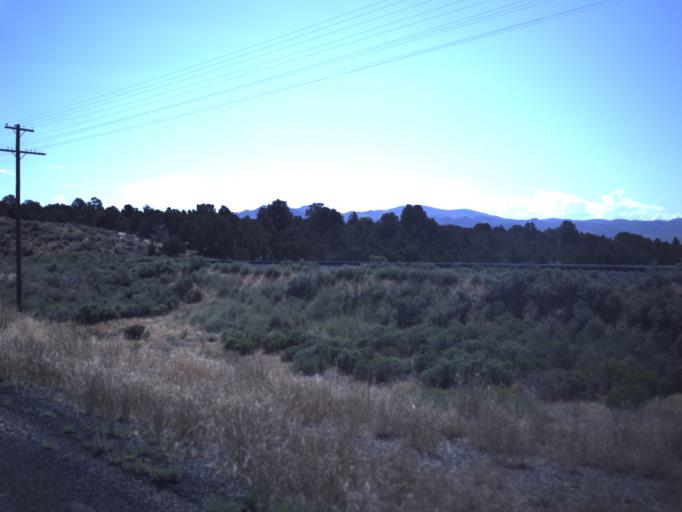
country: US
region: Utah
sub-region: Utah County
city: Genola
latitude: 39.9447
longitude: -112.2249
